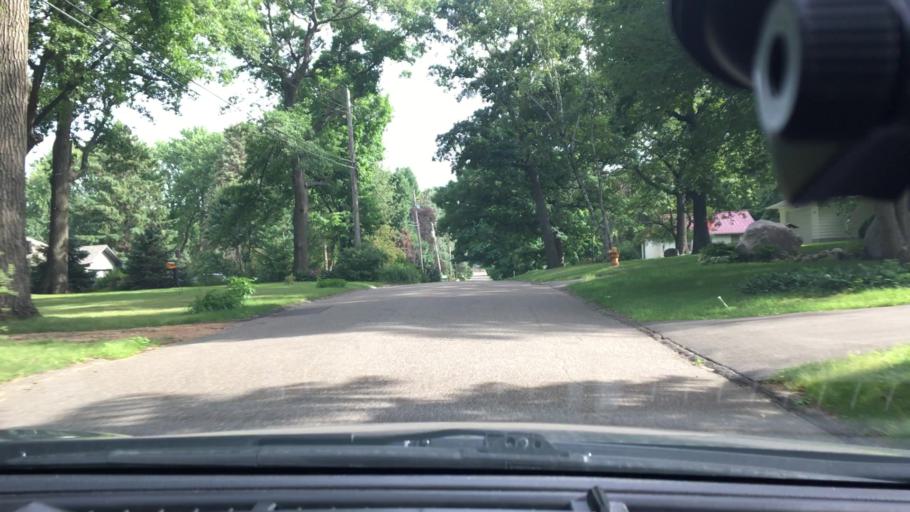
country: US
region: Minnesota
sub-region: Hennepin County
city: Plymouth
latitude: 45.0019
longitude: -93.4400
